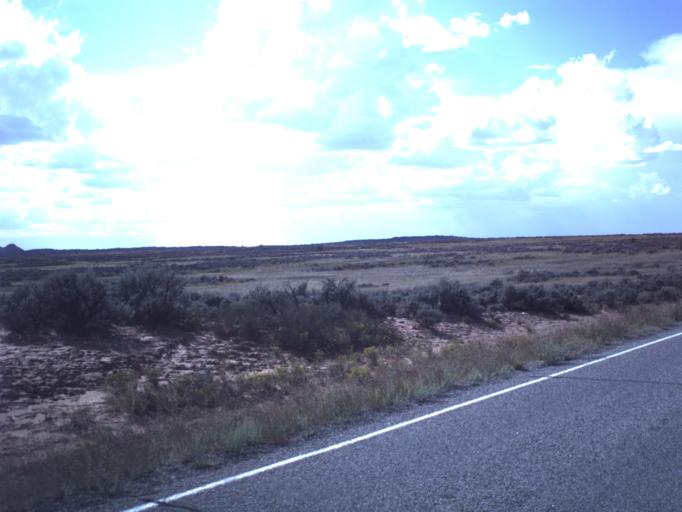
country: US
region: Utah
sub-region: Grand County
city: Moab
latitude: 38.5263
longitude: -109.7464
